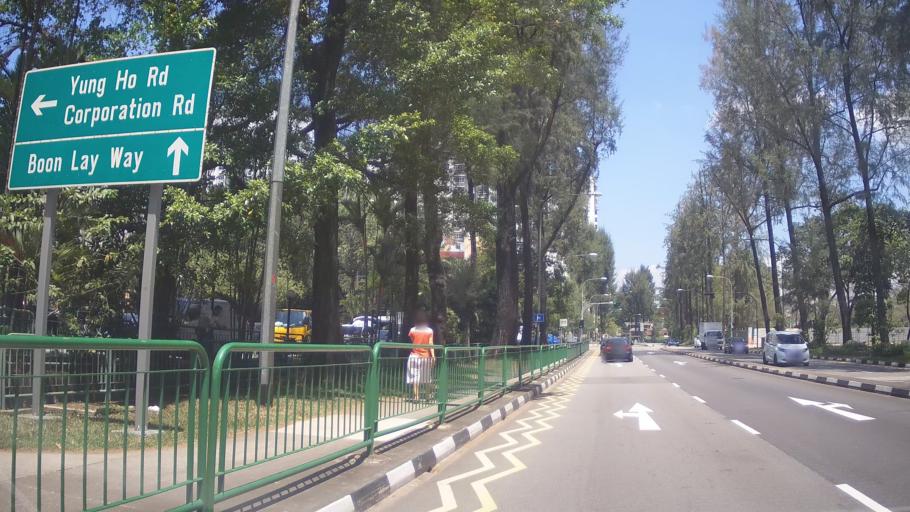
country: SG
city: Singapore
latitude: 1.3258
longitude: 103.7257
